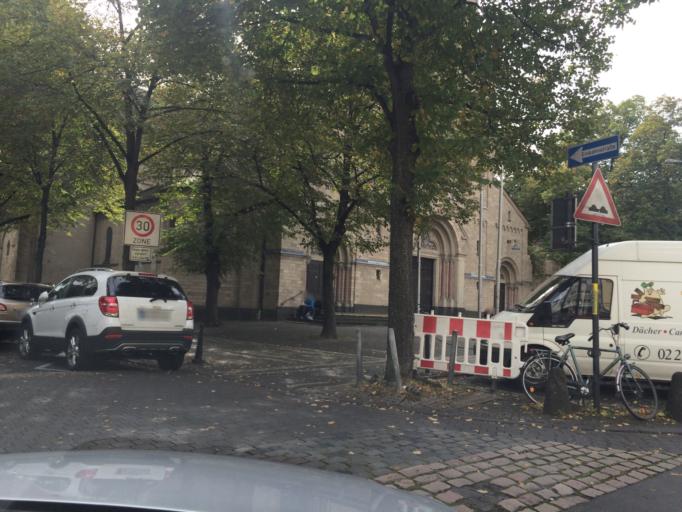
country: DE
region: North Rhine-Westphalia
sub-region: Regierungsbezirk Koln
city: Neustadt/Sued
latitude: 50.9195
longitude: 6.9267
